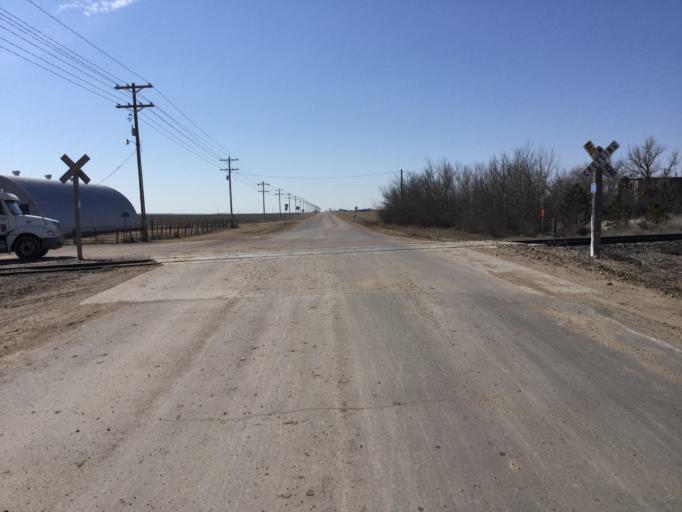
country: US
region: Kansas
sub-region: Stanton County
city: Johnson
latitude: 37.5209
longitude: -101.8890
